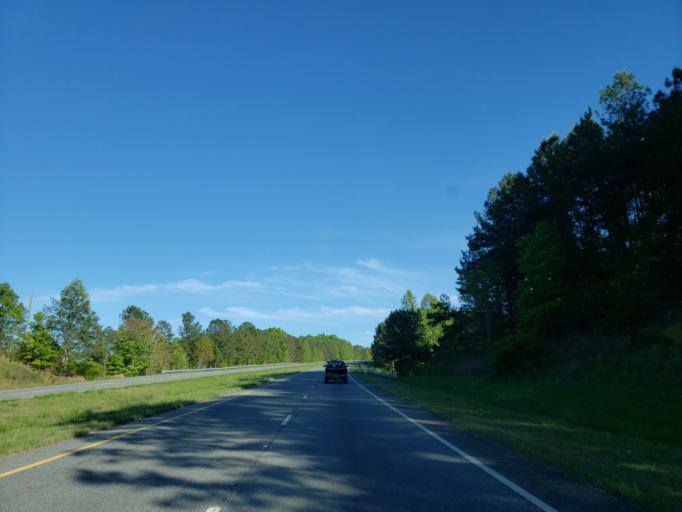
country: US
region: Georgia
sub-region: Polk County
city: Rockmart
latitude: 33.9641
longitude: -84.9917
